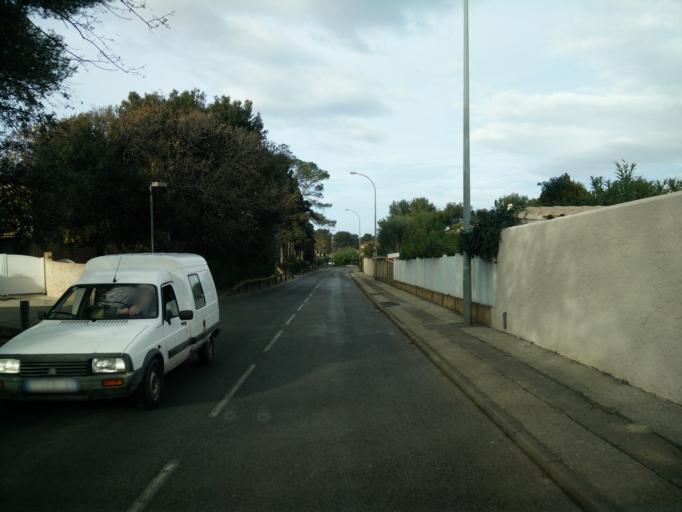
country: FR
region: Provence-Alpes-Cote d'Azur
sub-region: Departement du Var
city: Six-Fours-les-Plages
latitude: 43.0750
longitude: 5.8170
